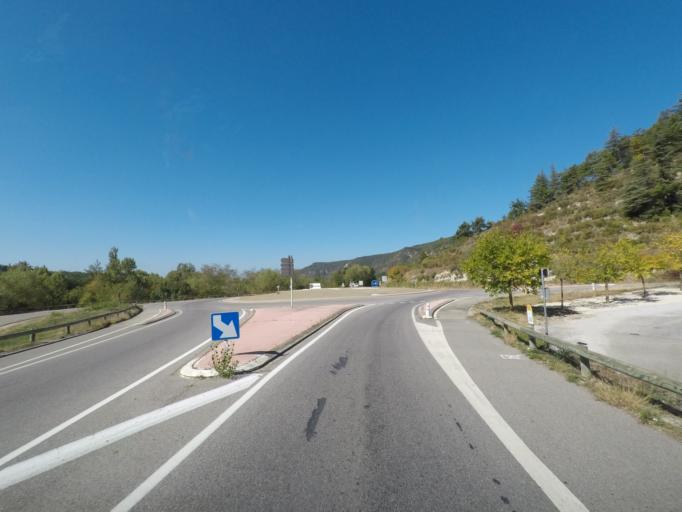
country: FR
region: Rhone-Alpes
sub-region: Departement de la Drome
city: Aouste-sur-Sye
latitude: 44.6936
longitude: 5.1710
